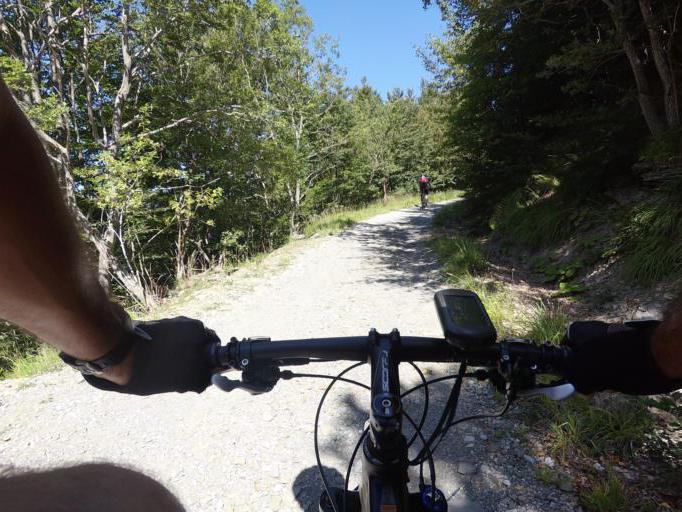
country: IT
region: Emilia-Romagna
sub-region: Provincia di Modena
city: Montecreto
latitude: 44.2282
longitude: 10.7293
